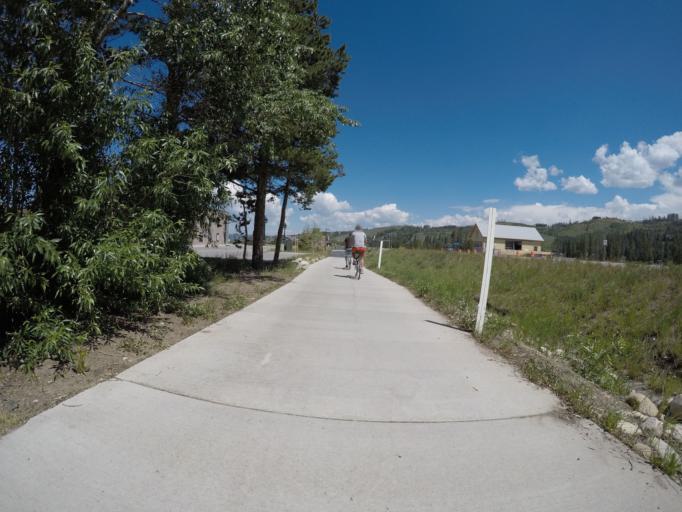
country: US
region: Colorado
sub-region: Grand County
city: Fraser
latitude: 39.9277
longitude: -105.7886
